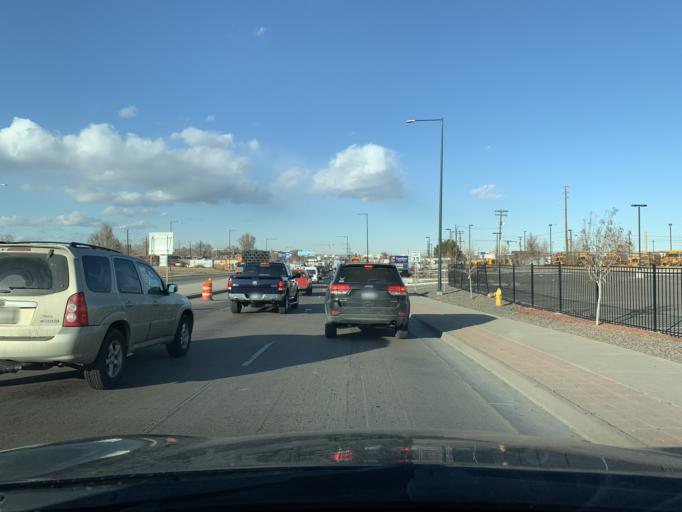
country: US
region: Colorado
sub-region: Denver County
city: Denver
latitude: 39.7261
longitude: -105.0249
